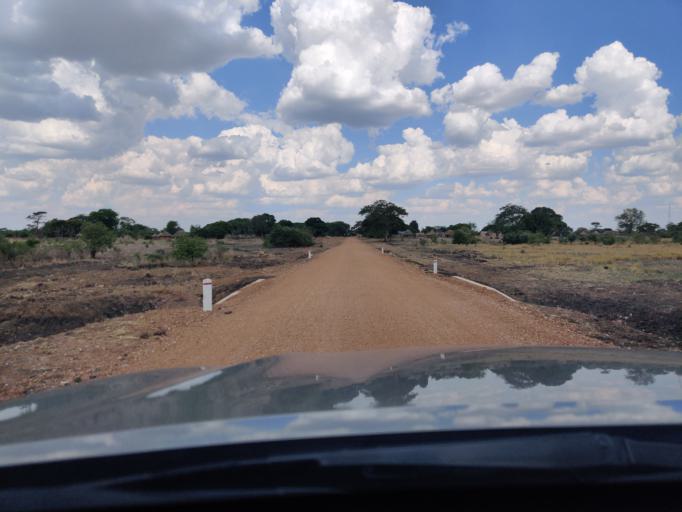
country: ZM
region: Central
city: Chibombo
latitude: -14.7616
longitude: 27.8927
